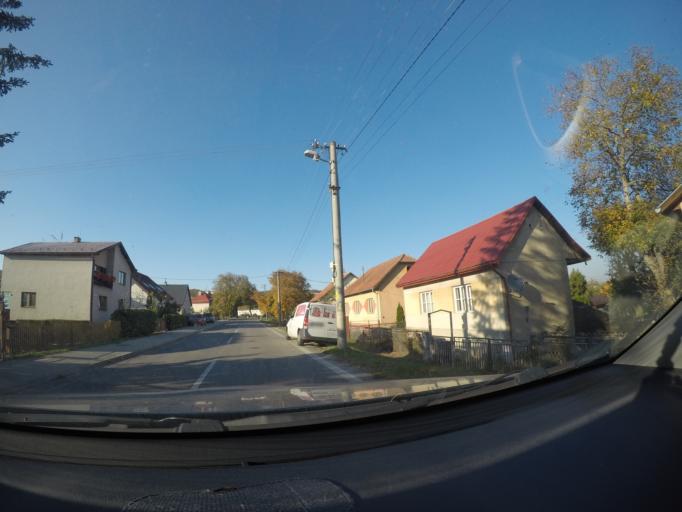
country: SK
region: Nitriansky
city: Nemsova
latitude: 48.9505
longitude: 18.0920
